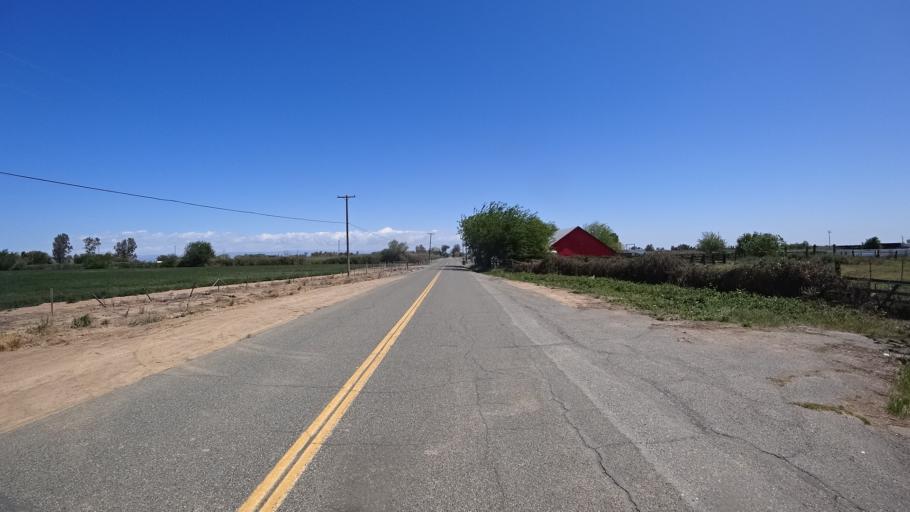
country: US
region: California
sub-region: Glenn County
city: Orland
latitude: 39.7944
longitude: -122.1993
